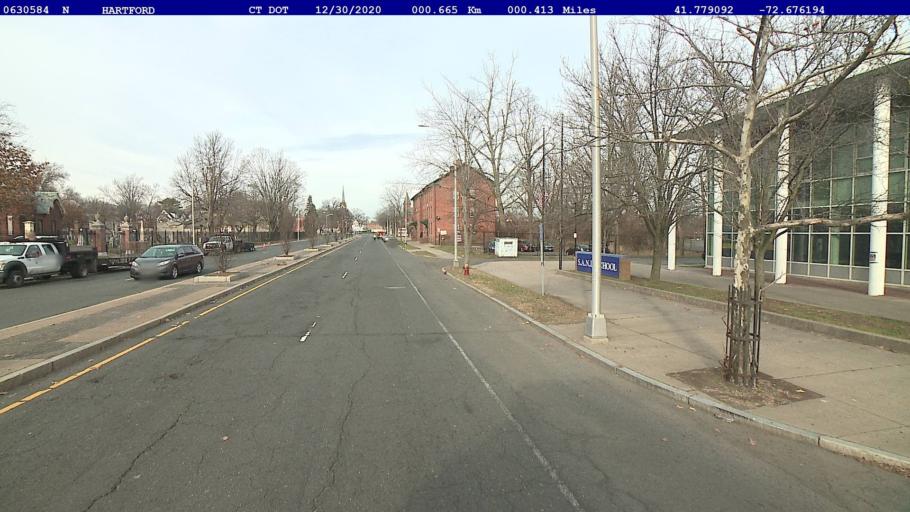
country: US
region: Connecticut
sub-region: Hartford County
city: Hartford
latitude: 41.7791
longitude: -72.6762
